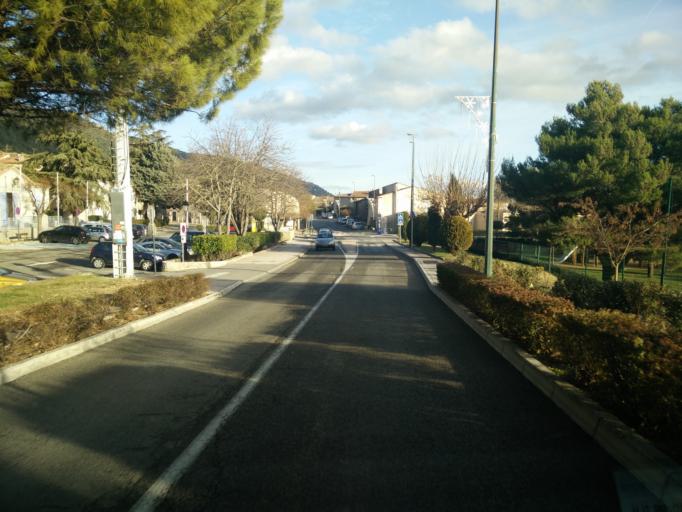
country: FR
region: Provence-Alpes-Cote d'Azur
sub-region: Departement du Var
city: Signes
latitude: 43.2902
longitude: 5.8610
